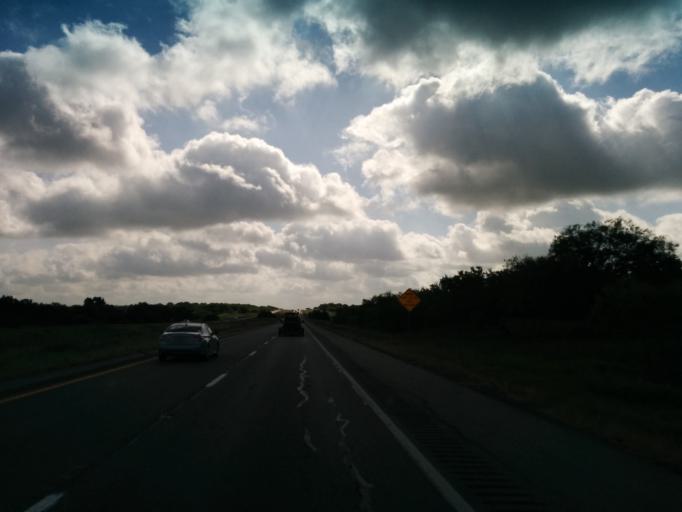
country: US
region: Texas
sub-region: Caldwell County
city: Luling
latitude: 29.6370
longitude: -97.7264
